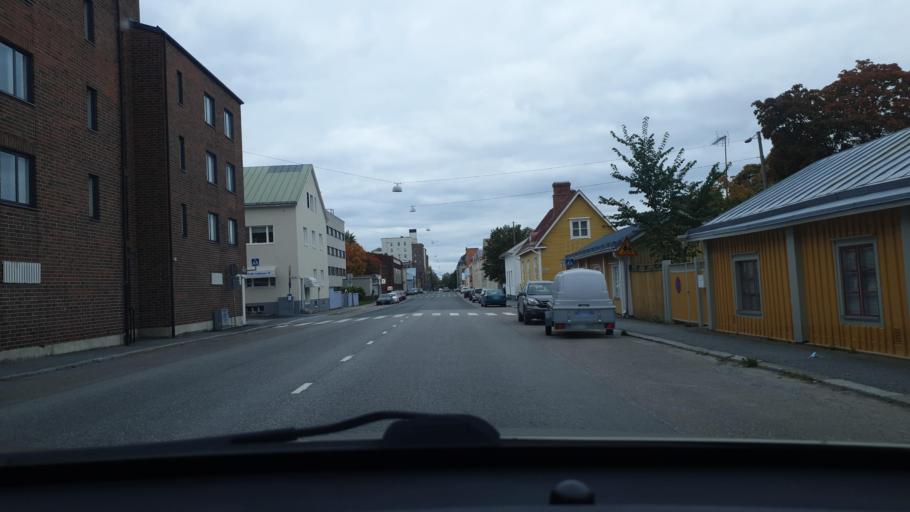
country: FI
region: Ostrobothnia
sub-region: Vaasa
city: Vaasa
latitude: 63.0921
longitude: 21.6257
